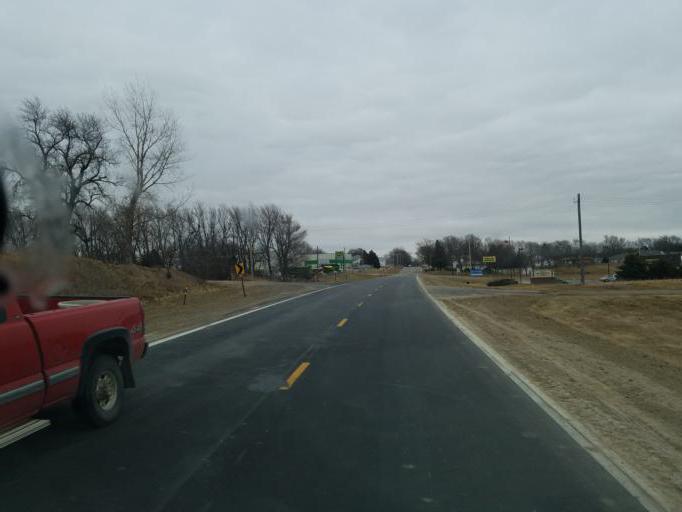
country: US
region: Nebraska
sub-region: Knox County
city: Bloomfield
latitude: 42.5997
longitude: -97.6586
